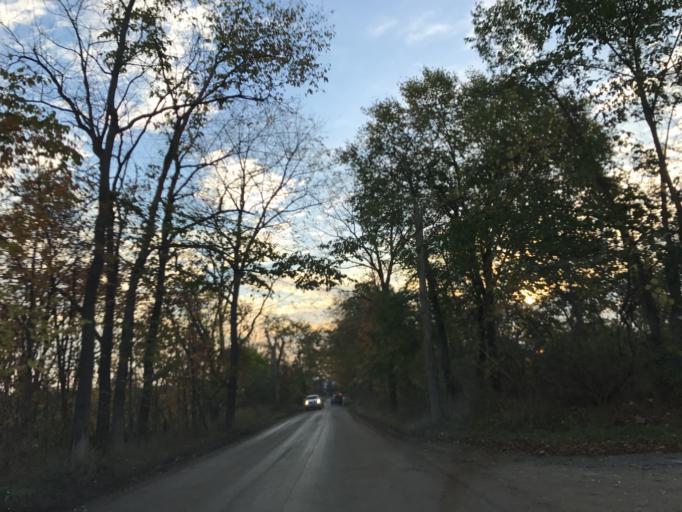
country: US
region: Michigan
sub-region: Oakland County
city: Wixom
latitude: 42.4783
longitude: -83.5577
